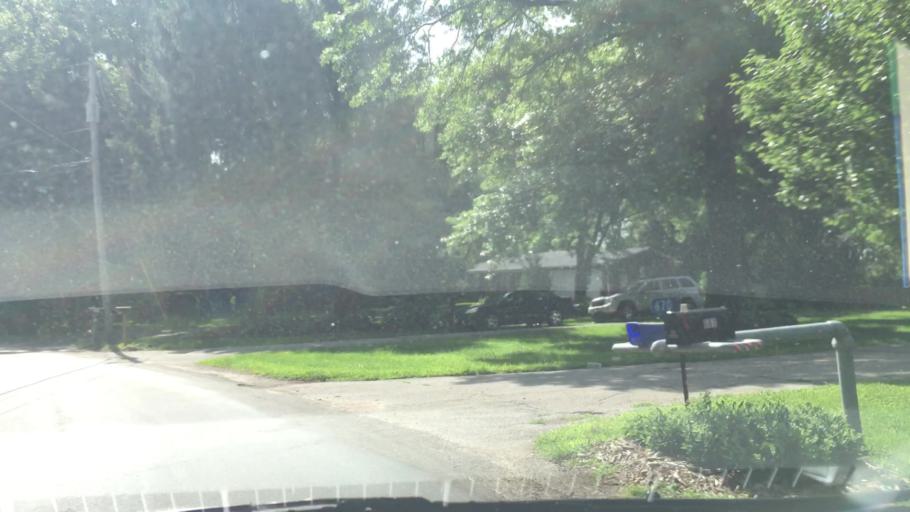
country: US
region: Iowa
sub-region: Johnson County
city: Iowa City
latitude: 41.6892
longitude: -91.5325
